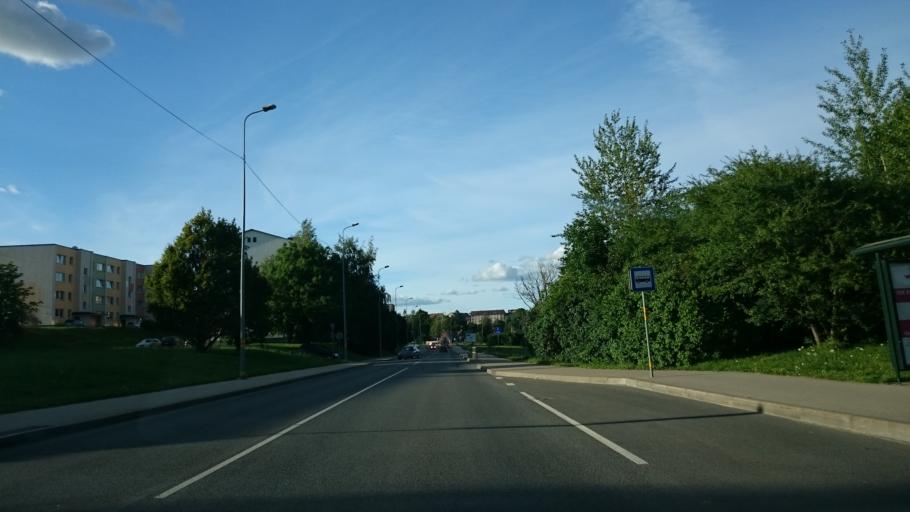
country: LV
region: Saldus Rajons
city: Saldus
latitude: 56.6606
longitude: 22.4758
